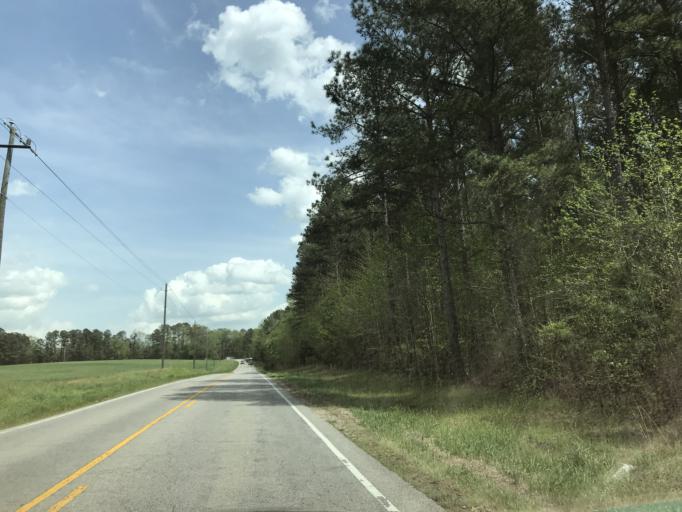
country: US
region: North Carolina
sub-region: Nash County
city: Spring Hope
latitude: 35.9693
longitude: -78.2148
